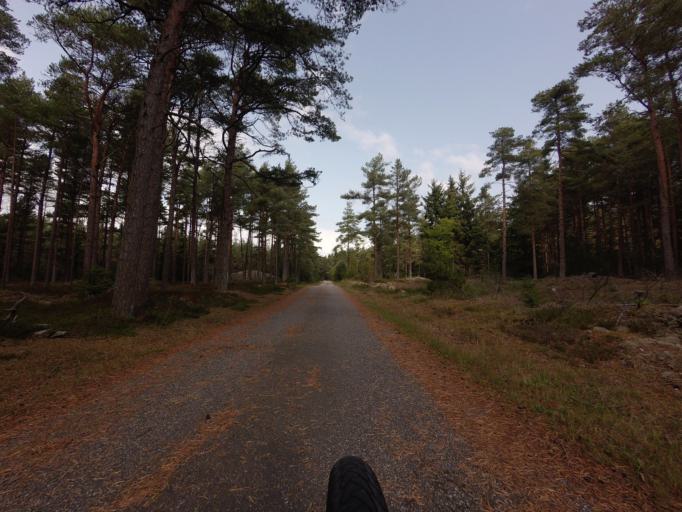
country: DK
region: North Denmark
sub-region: Frederikshavn Kommune
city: Strandby
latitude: 57.6343
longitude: 10.4341
